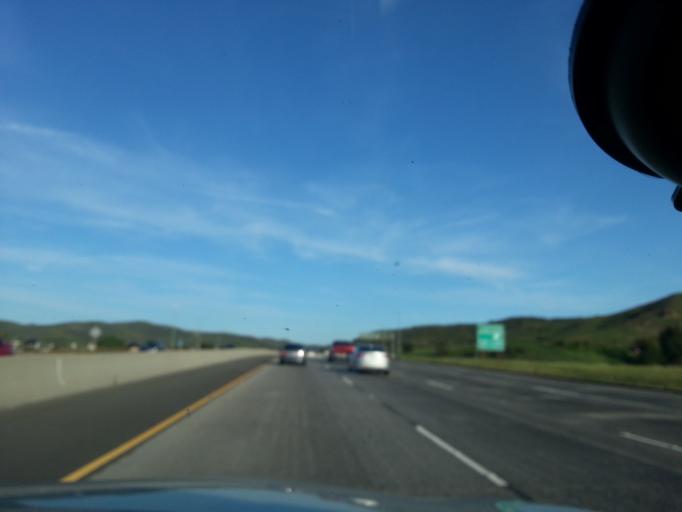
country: US
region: California
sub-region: Ventura County
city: Thousand Oaks
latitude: 34.1765
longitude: -118.8648
